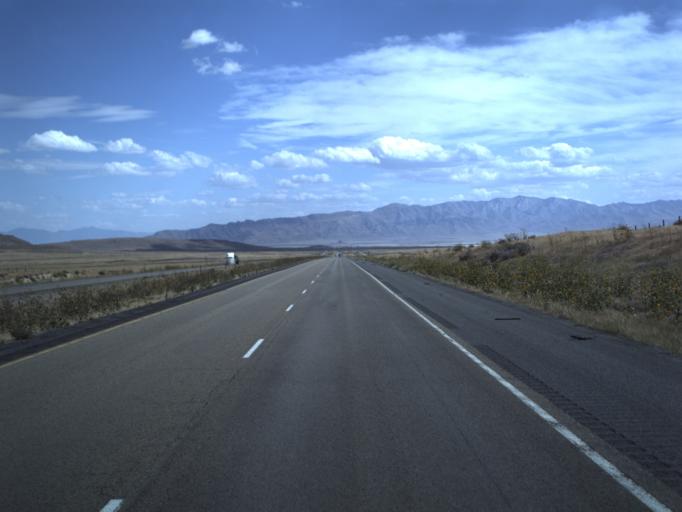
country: US
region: Utah
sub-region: Tooele County
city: Grantsville
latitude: 40.8113
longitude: -112.8704
